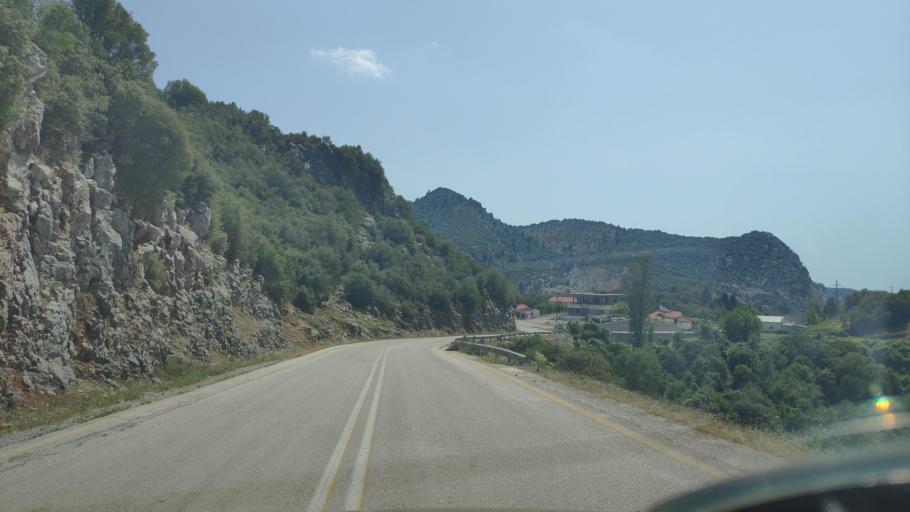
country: GR
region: Epirus
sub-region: Nomos Artas
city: Ano Kalentini
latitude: 39.2575
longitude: 21.2475
